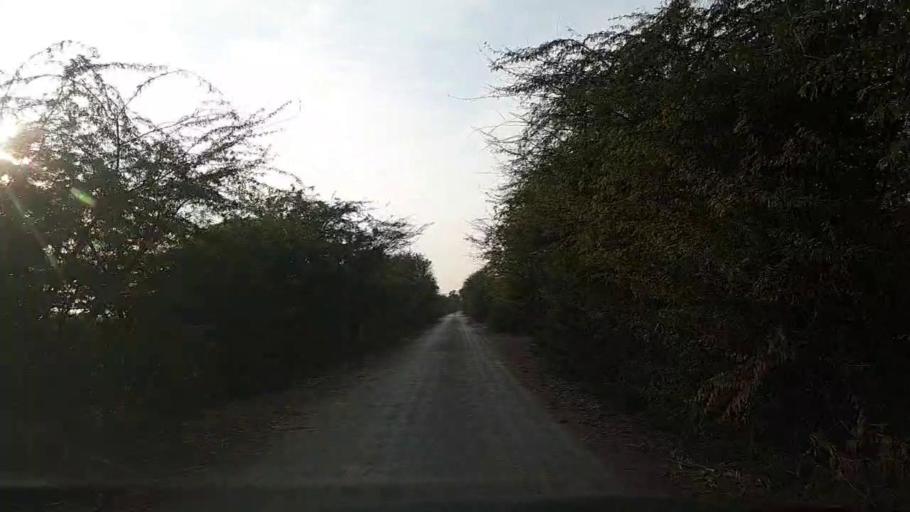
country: PK
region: Sindh
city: Jam Sahib
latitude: 26.4318
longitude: 68.5707
